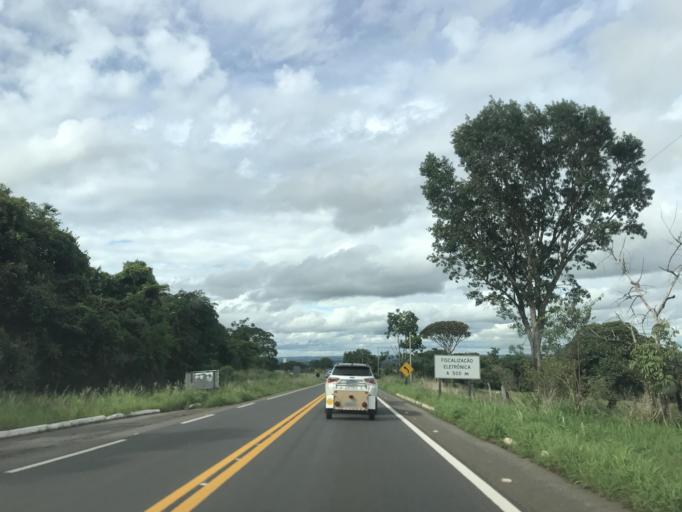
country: BR
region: Goias
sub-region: Piracanjuba
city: Piracanjuba
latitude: -17.2134
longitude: -48.7087
